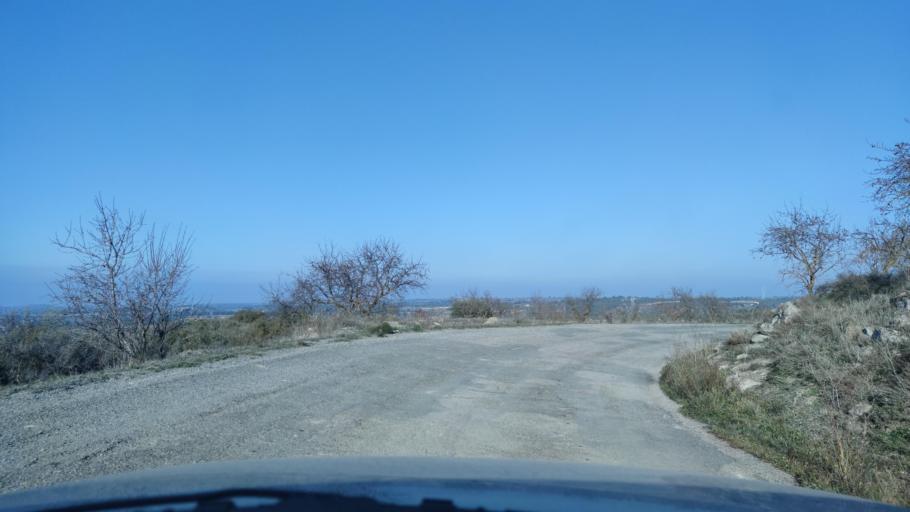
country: ES
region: Catalonia
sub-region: Provincia de Lleida
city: Maials
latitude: 41.3769
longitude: 0.5575
